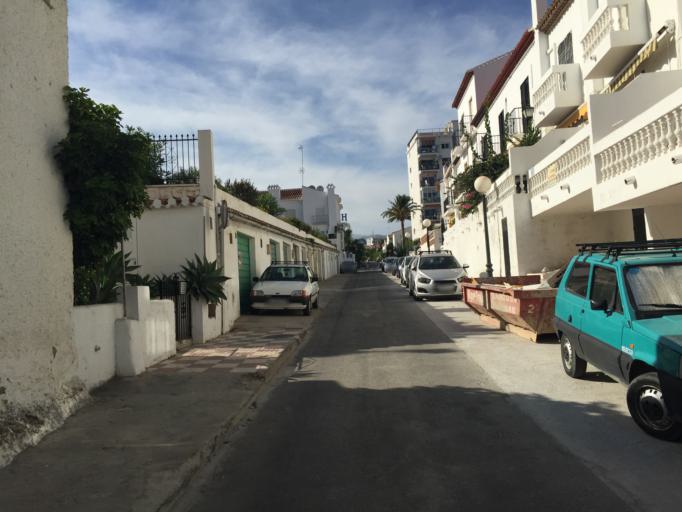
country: ES
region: Andalusia
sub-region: Provincia de Malaga
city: Nerja
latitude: 36.7518
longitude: -3.8712
